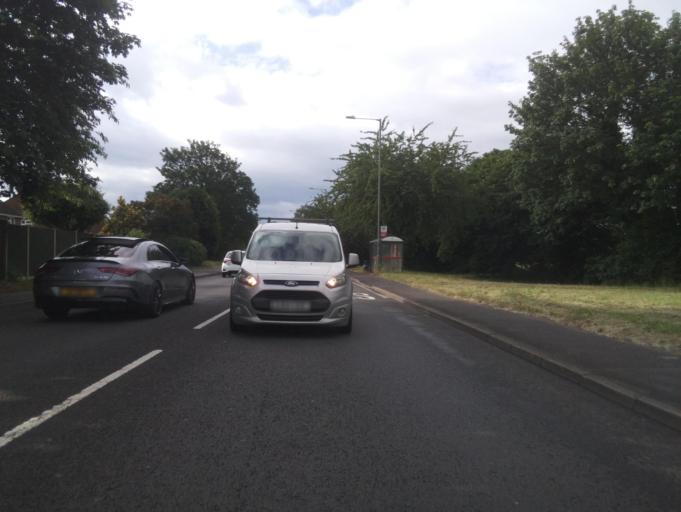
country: GB
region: England
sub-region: Dudley
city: Kingswinford
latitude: 52.5092
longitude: -2.1726
